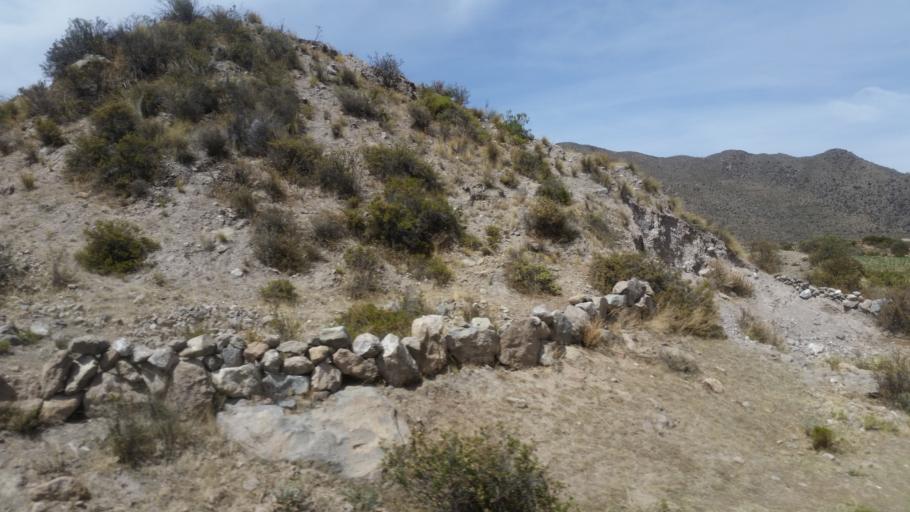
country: PE
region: Arequipa
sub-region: Provincia de Caylloma
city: Madrigal
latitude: -15.6183
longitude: -71.8578
